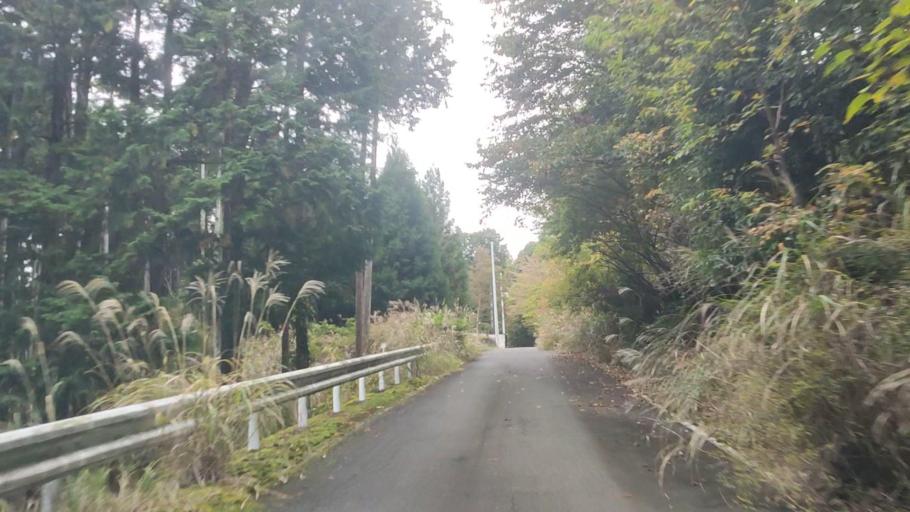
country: JP
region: Shizuoka
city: Ito
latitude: 34.9207
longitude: 138.9829
